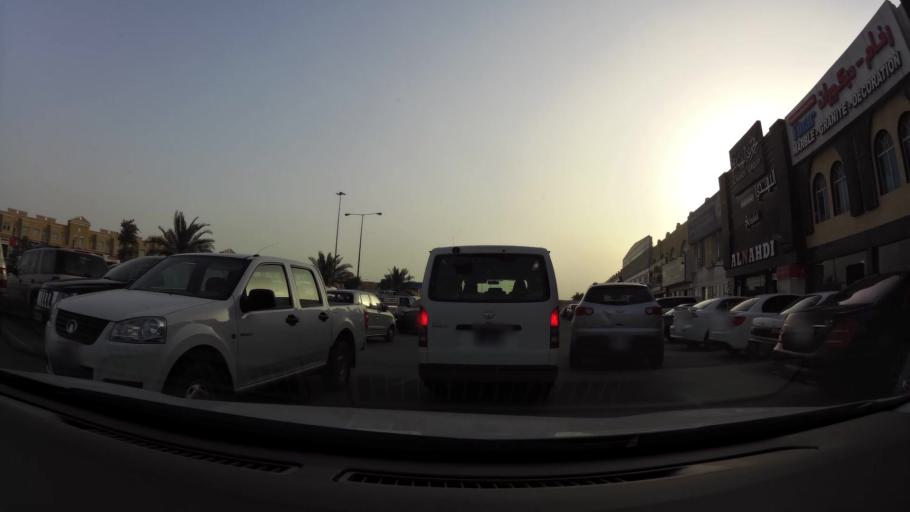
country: QA
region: Baladiyat ar Rayyan
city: Ar Rayyan
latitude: 25.2405
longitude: 51.4560
